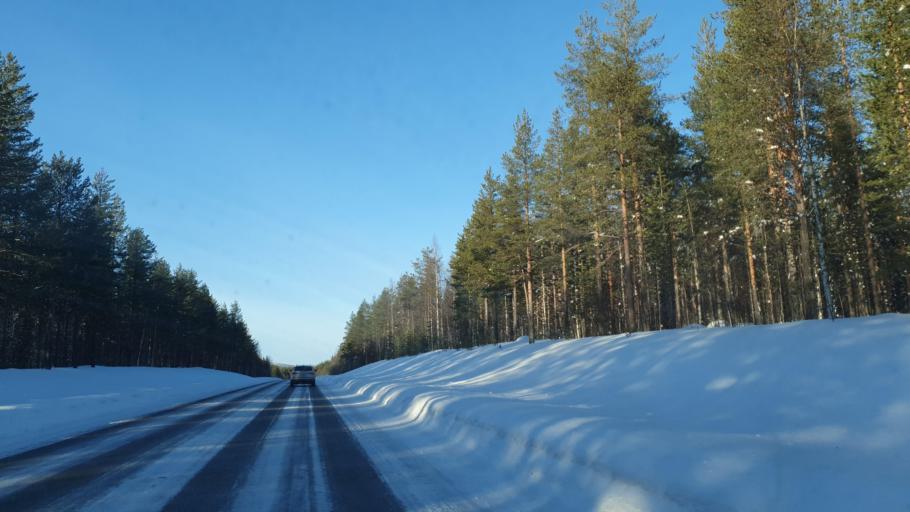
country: FI
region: Lapland
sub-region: Torniolaakso
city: Pello
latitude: 67.0813
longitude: 24.0121
